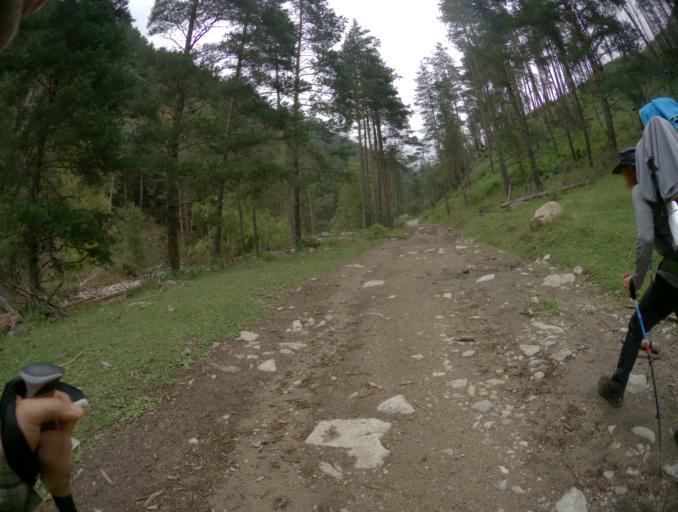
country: RU
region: Karachayevo-Cherkesiya
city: Uchkulan
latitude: 43.4199
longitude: 42.2179
